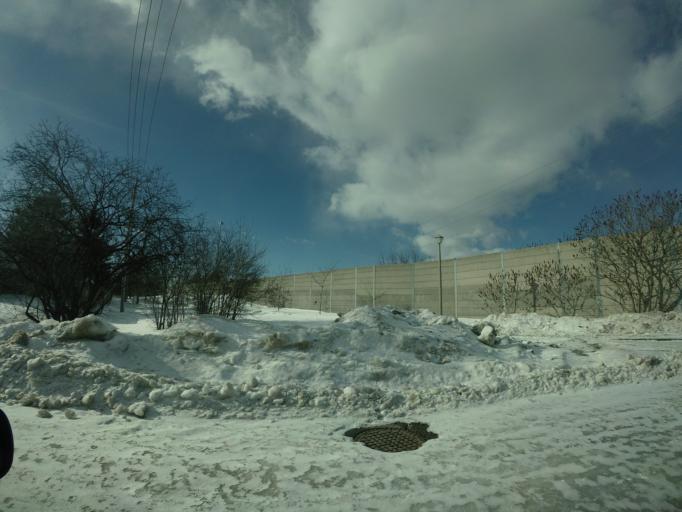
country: CA
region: Ontario
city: Ottawa
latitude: 45.4283
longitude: -75.6111
